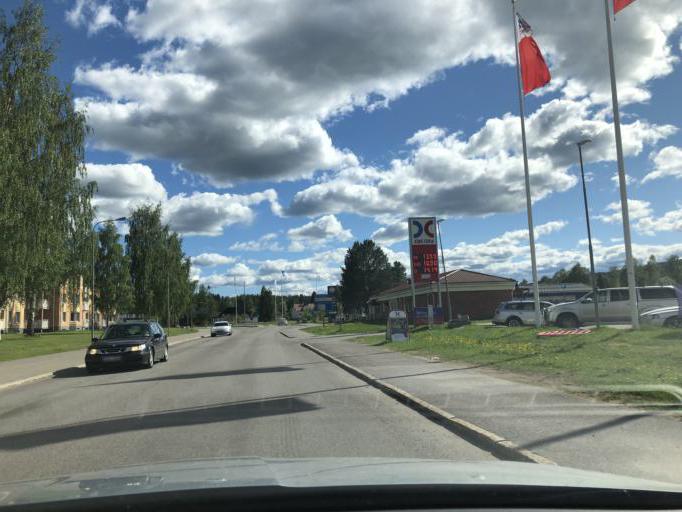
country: SE
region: Norrbotten
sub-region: Alvsbyns Kommun
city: AElvsbyn
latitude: 65.6731
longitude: 21.0059
